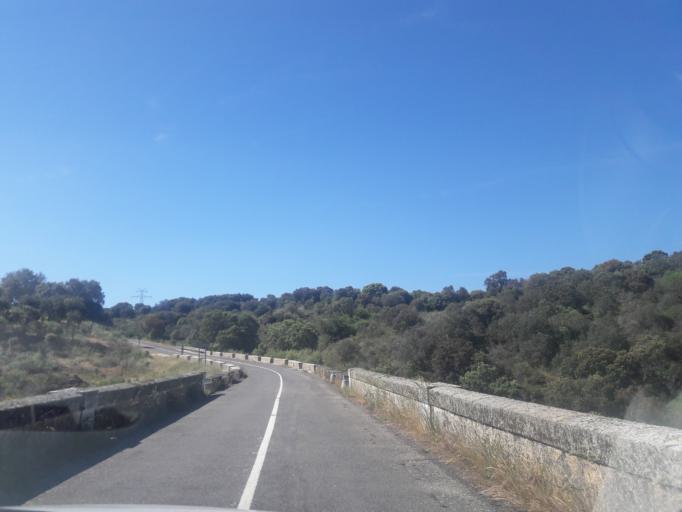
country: ES
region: Castille and Leon
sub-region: Provincia de Salamanca
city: Saucelle
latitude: 41.0070
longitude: -6.7357
